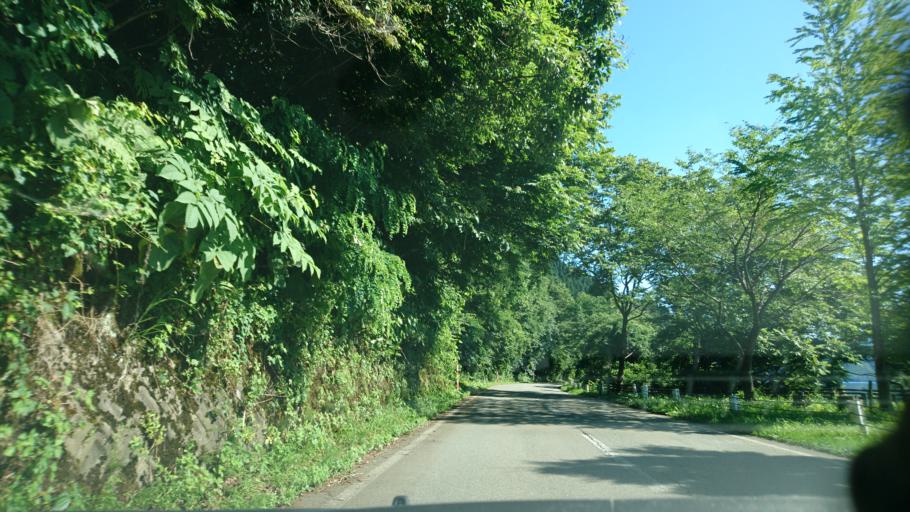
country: JP
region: Akita
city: Kakunodatemachi
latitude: 39.7227
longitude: 140.6279
